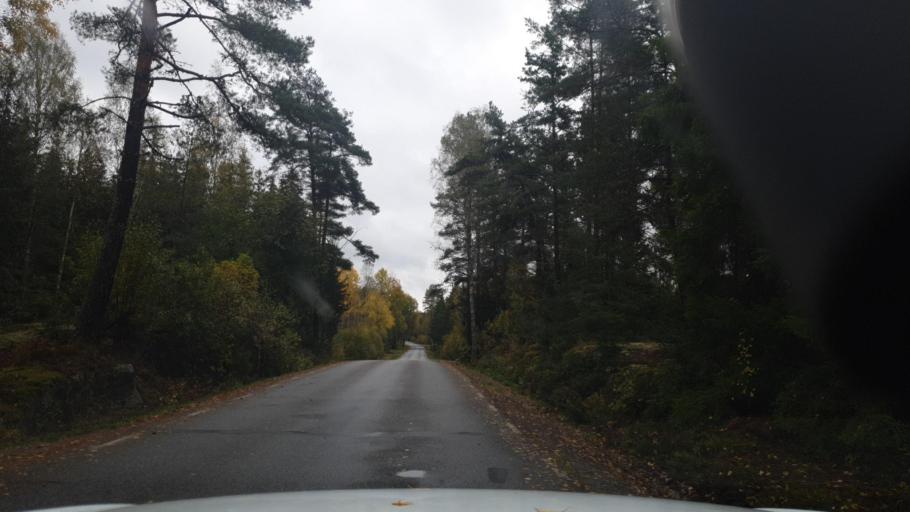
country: SE
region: Vaermland
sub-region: Karlstads Kommun
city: Valberg
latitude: 59.4178
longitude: 13.1198
